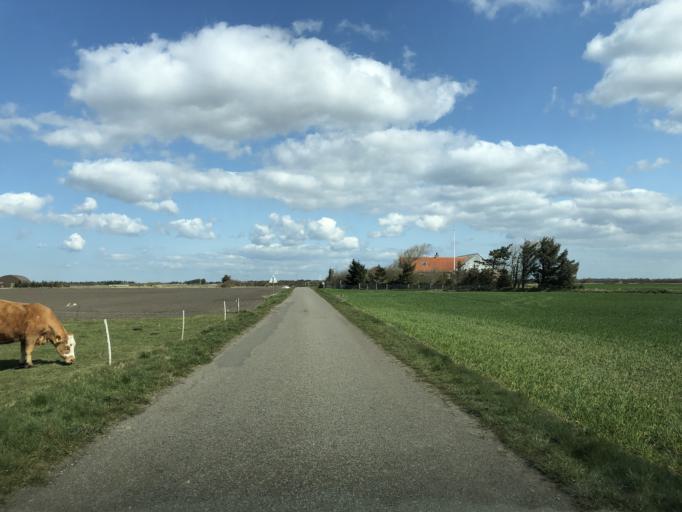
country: DK
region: Central Jutland
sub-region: Holstebro Kommune
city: Ulfborg
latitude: 56.4004
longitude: 8.1762
